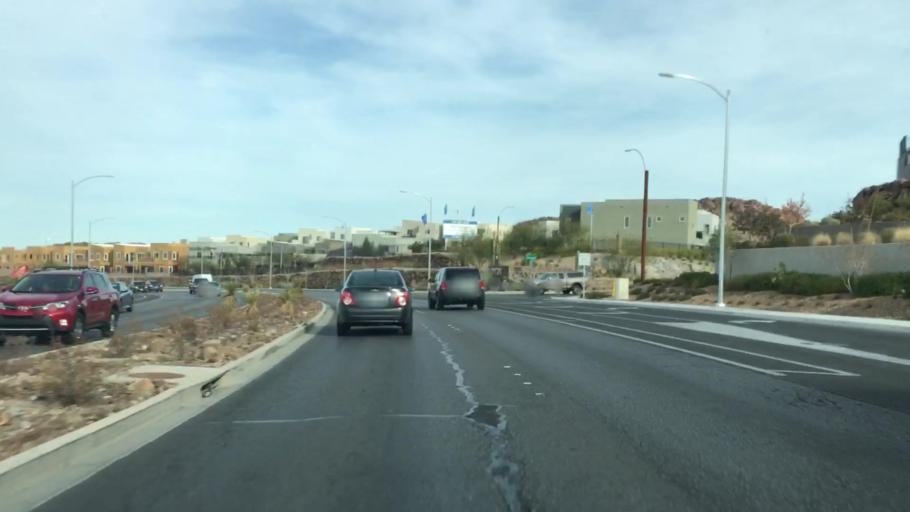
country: US
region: Nevada
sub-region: Clark County
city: Whitney
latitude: 35.9982
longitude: -115.0851
